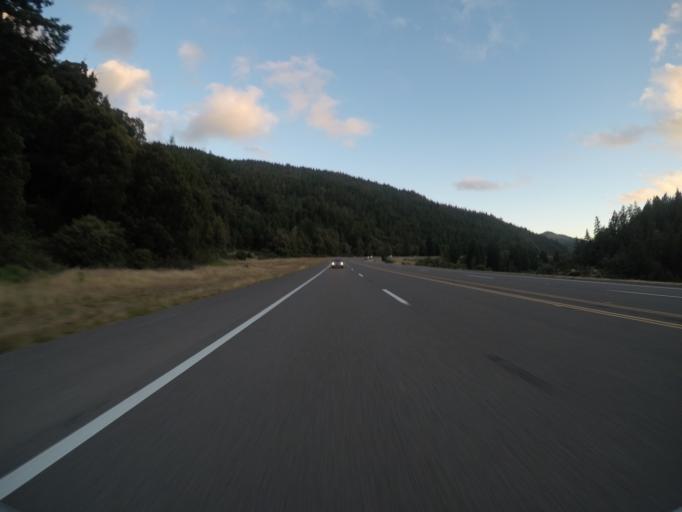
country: US
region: California
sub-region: Humboldt County
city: Redway
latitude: 39.9941
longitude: -123.7885
